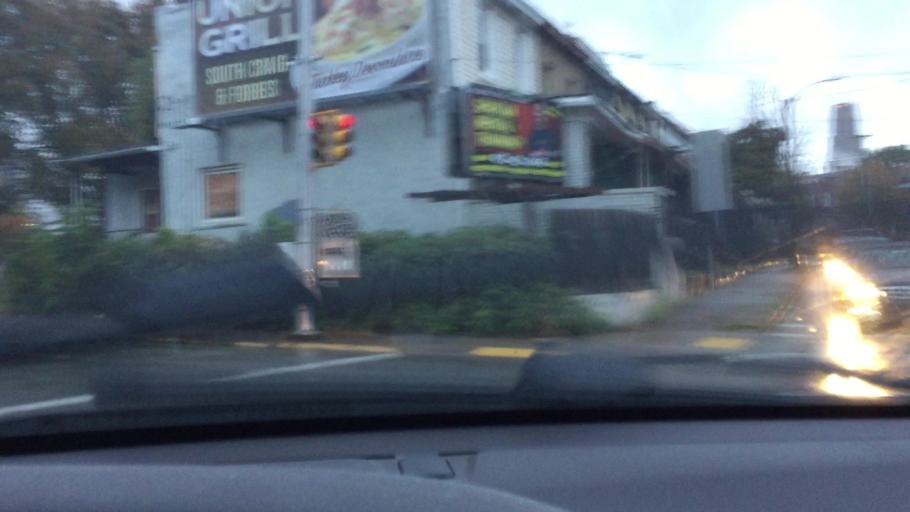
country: US
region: Pennsylvania
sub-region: Allegheny County
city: Bloomfield
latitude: 40.4352
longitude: -79.9565
